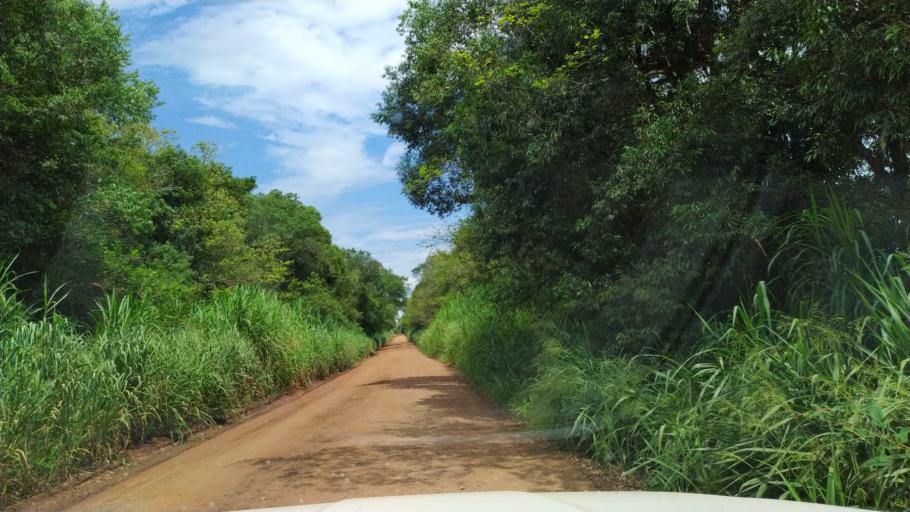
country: AR
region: Misiones
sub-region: Departamento de Eldorado
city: Eldorado
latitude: -26.4658
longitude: -54.5933
